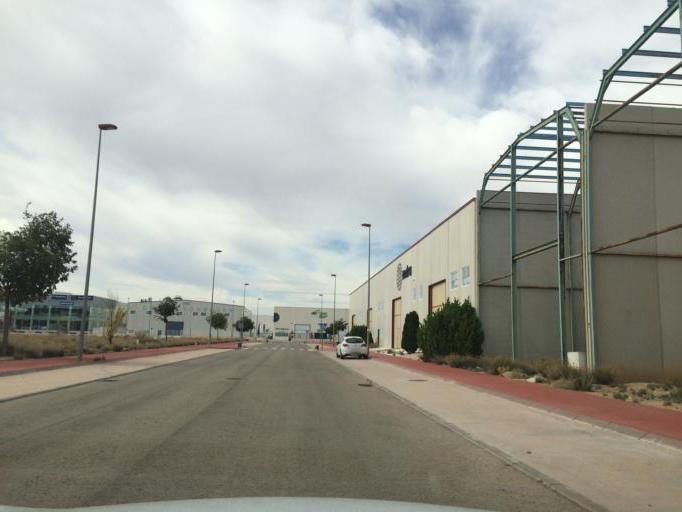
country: ES
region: Castille-La Mancha
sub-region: Provincia de Albacete
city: Albacete
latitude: 39.0276
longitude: -1.8885
